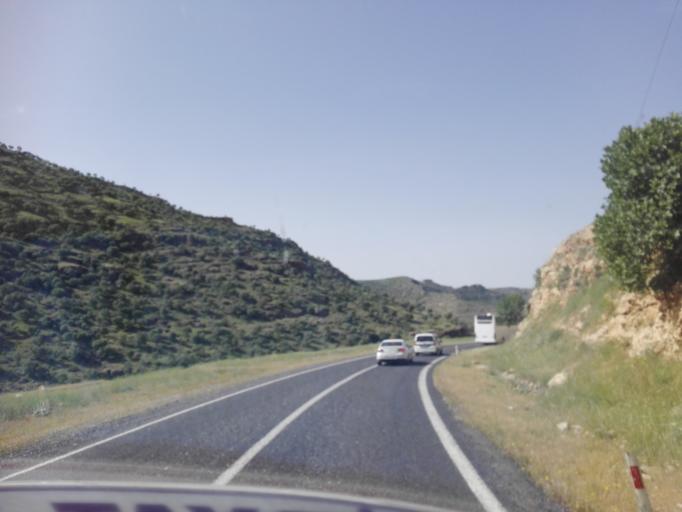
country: TR
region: Mardin
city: Sivrice
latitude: 37.2588
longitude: 41.3603
